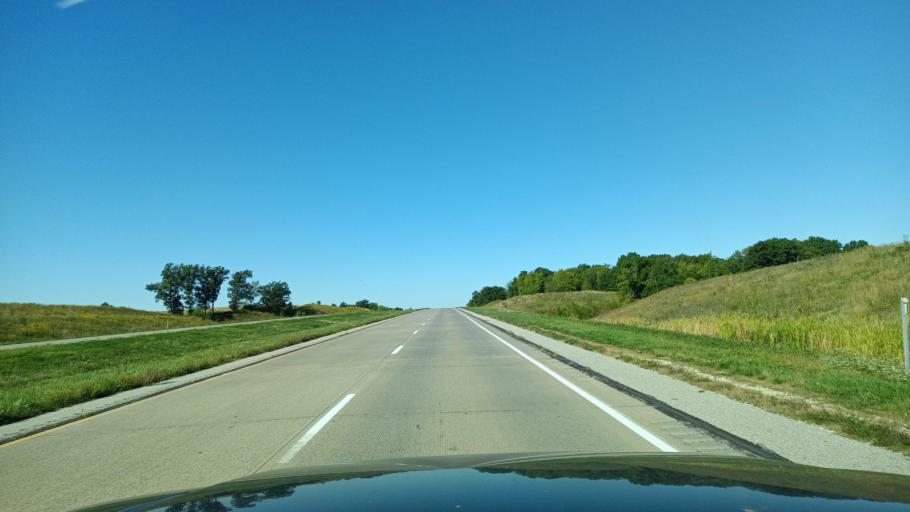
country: US
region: Iowa
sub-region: Lee County
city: Fort Madison
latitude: 40.6707
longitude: -91.3023
